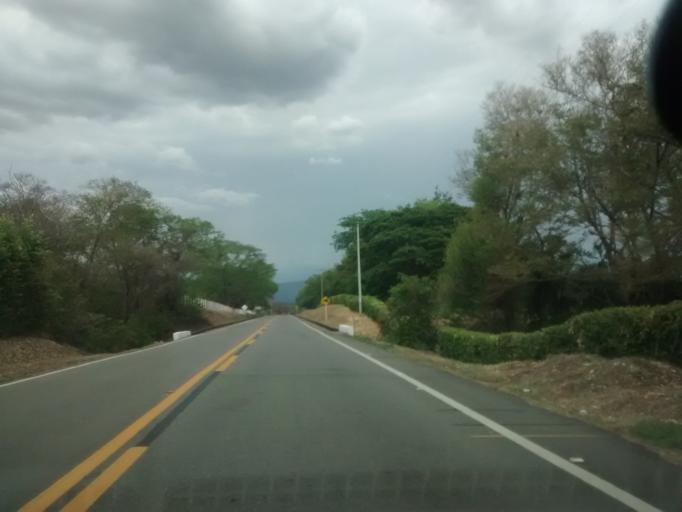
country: CO
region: Cundinamarca
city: Agua de Dios
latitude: 4.4095
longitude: -74.7136
